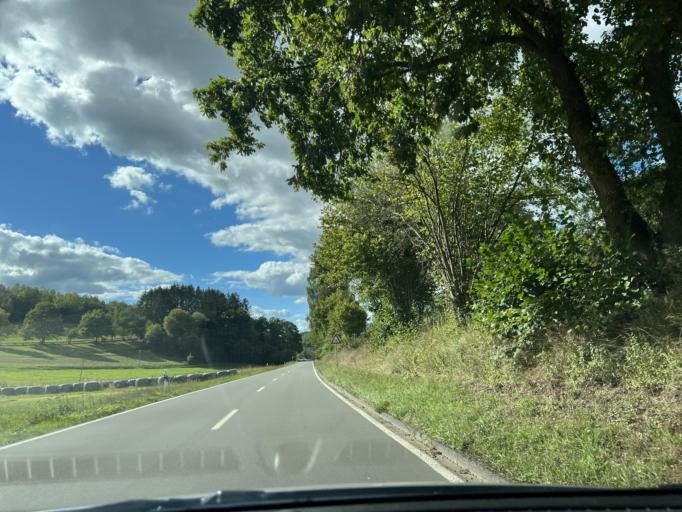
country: DE
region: North Rhine-Westphalia
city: Hilchenbach
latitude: 50.9712
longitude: 8.1272
